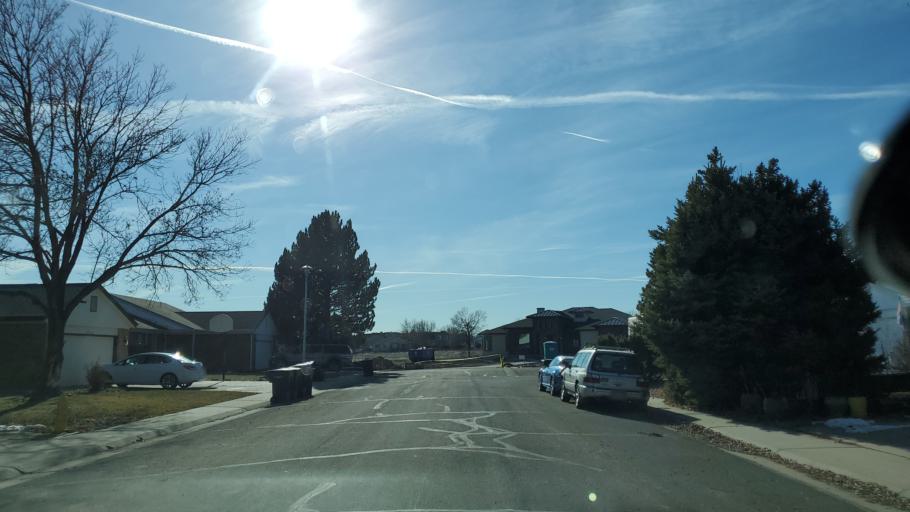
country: US
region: Colorado
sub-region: Adams County
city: Northglenn
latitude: 39.9199
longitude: -104.9530
